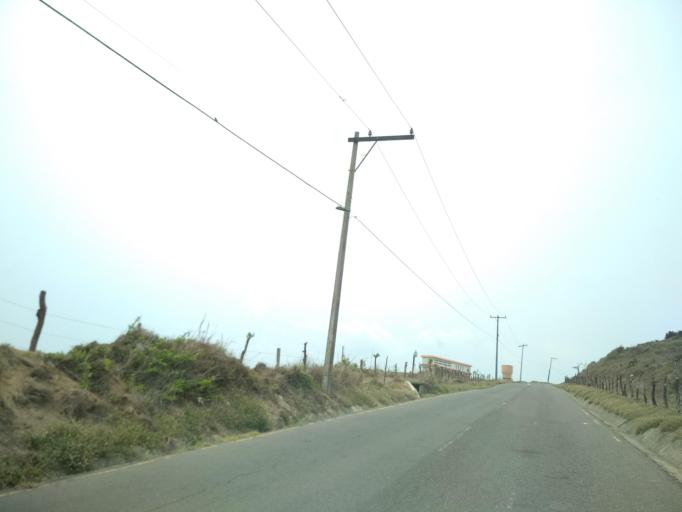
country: MX
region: Veracruz
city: Anton Lizardo
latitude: 19.0500
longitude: -96.0308
